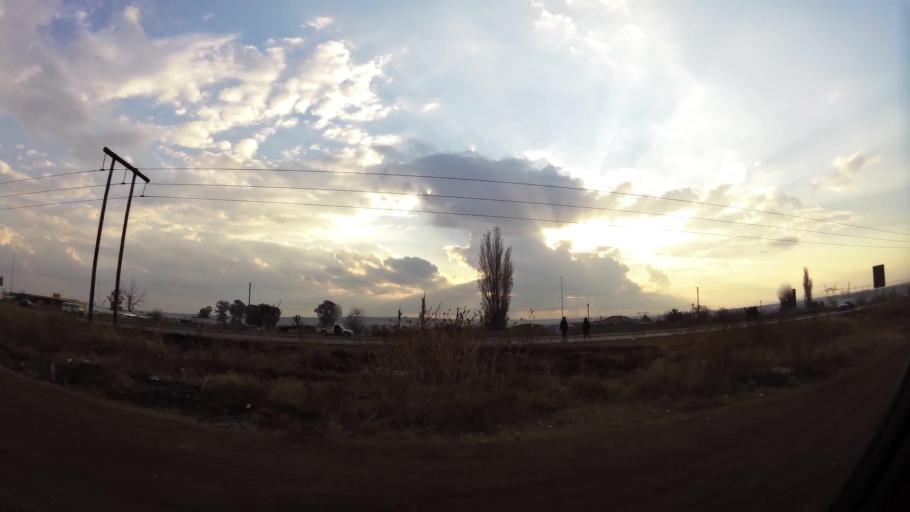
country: ZA
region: Gauteng
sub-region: City of Johannesburg Metropolitan Municipality
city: Orange Farm
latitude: -26.5547
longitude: 27.8304
